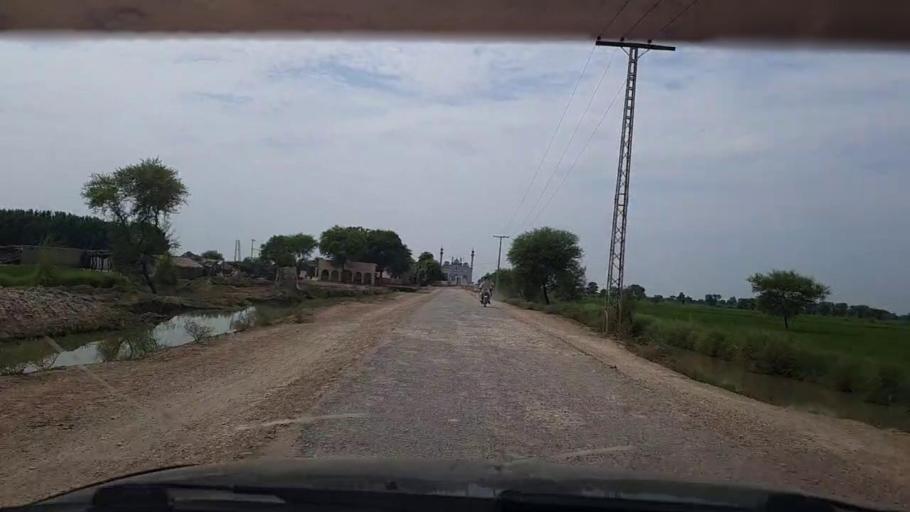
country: PK
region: Sindh
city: Thul
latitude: 28.2435
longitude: 68.7341
